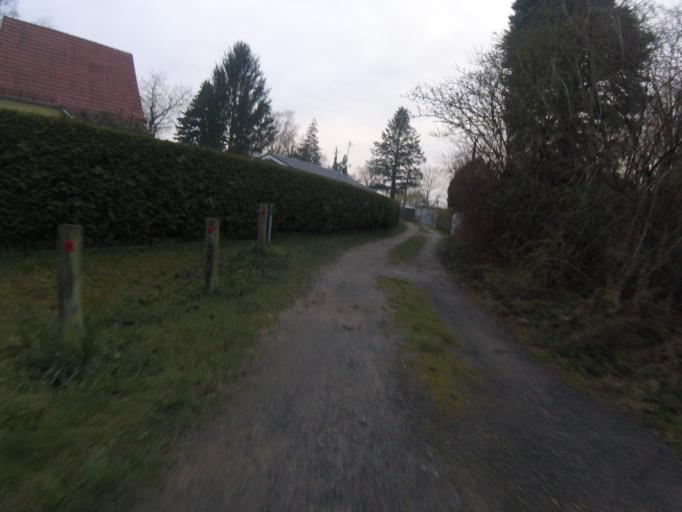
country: DE
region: Brandenburg
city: Konigs Wusterhausen
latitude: 52.2937
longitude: 13.6704
